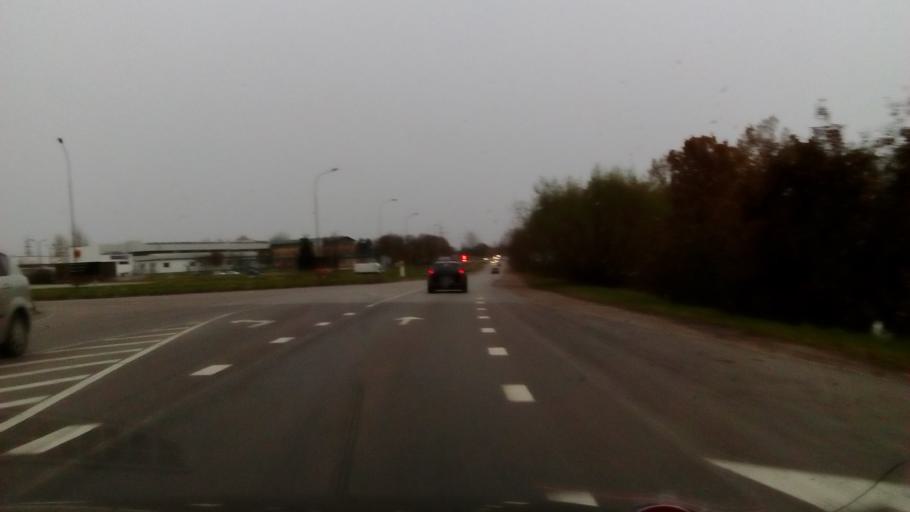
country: LT
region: Alytaus apskritis
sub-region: Alytus
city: Alytus
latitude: 54.4272
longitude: 24.0013
